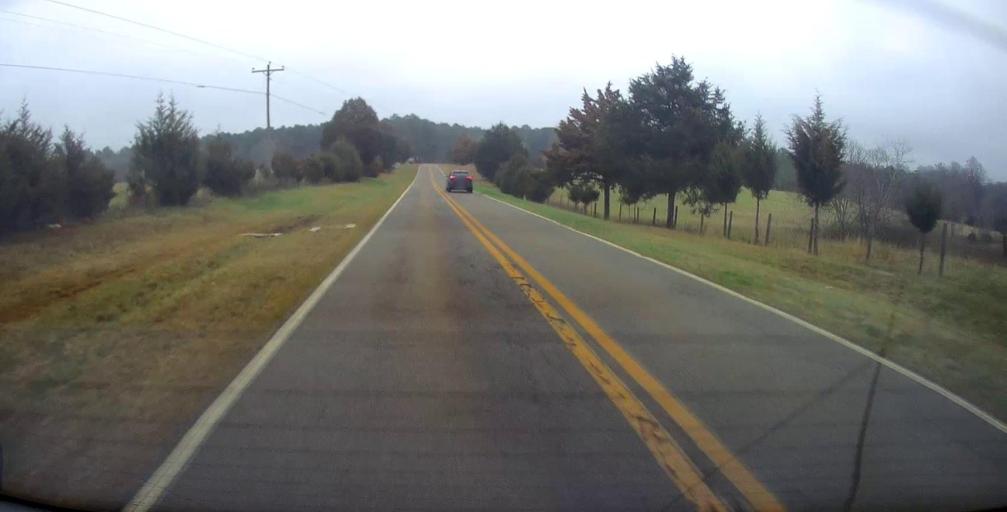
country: US
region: Georgia
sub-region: Lamar County
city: Barnesville
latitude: 33.1083
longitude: -84.0443
